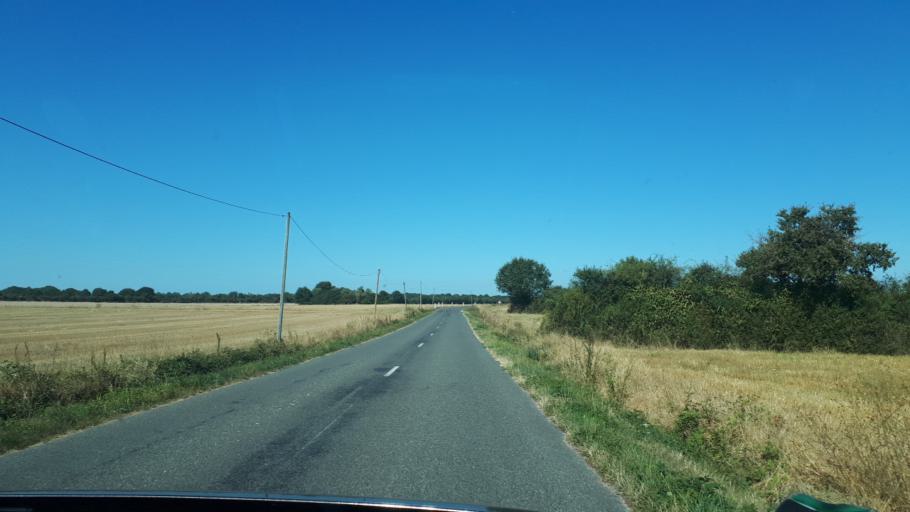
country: FR
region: Centre
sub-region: Departement du Loiret
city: Autry-le-Chatel
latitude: 47.6104
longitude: 2.5622
